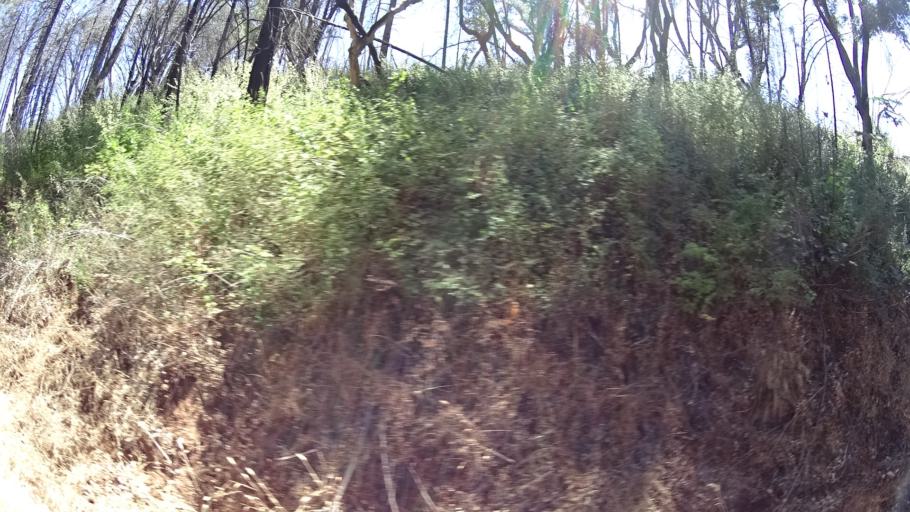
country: US
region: California
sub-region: Calaveras County
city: Mountain Ranch
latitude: 38.2570
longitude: -120.5805
